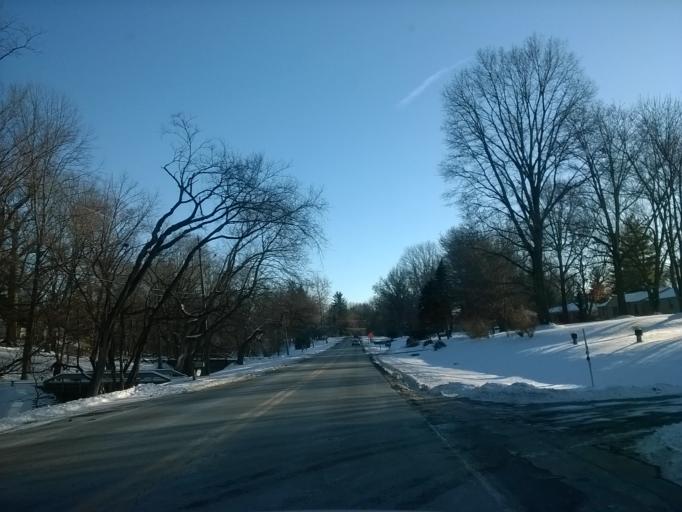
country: US
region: Indiana
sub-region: Marion County
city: Meridian Hills
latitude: 39.8998
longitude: -86.1364
